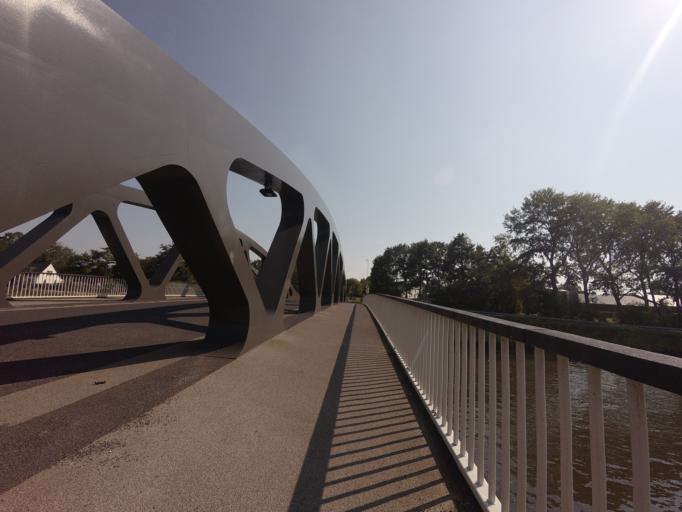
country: NL
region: Groningen
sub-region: Gemeente Zuidhorn
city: Noordhorn
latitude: 53.2554
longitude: 6.3996
